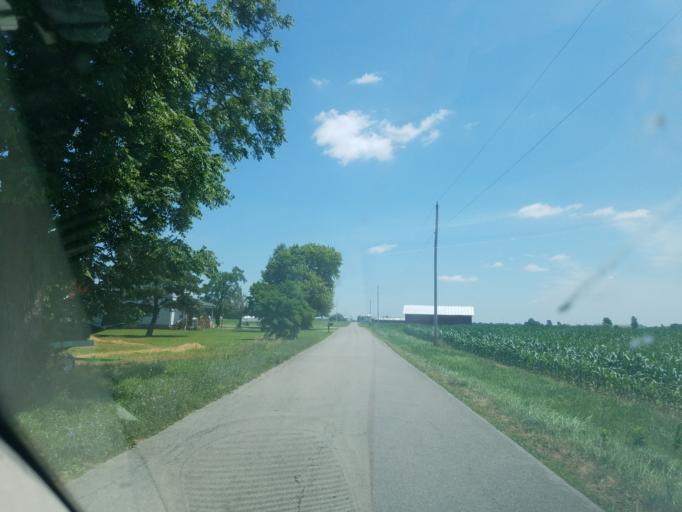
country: US
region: Ohio
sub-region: Hancock County
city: Arlington
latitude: 40.8495
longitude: -83.5941
